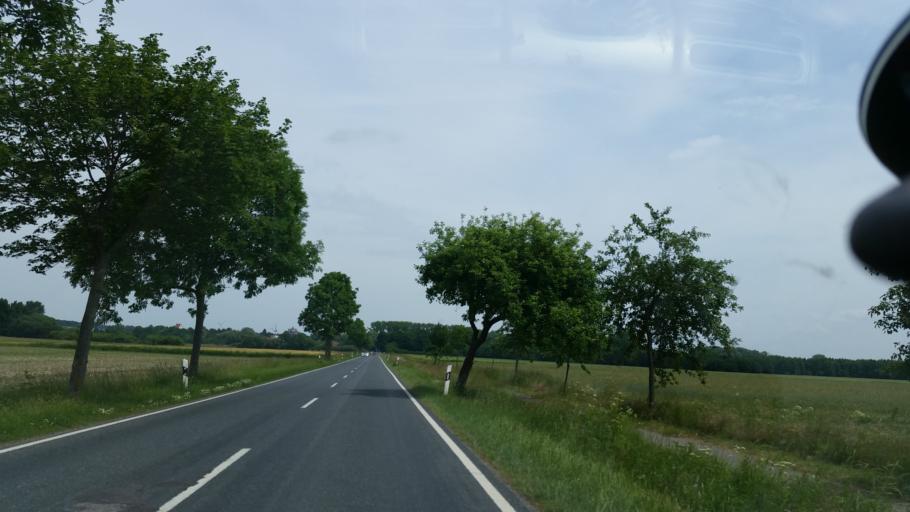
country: DE
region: Lower Saxony
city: Konigslutter am Elm
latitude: 52.2993
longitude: 10.7995
